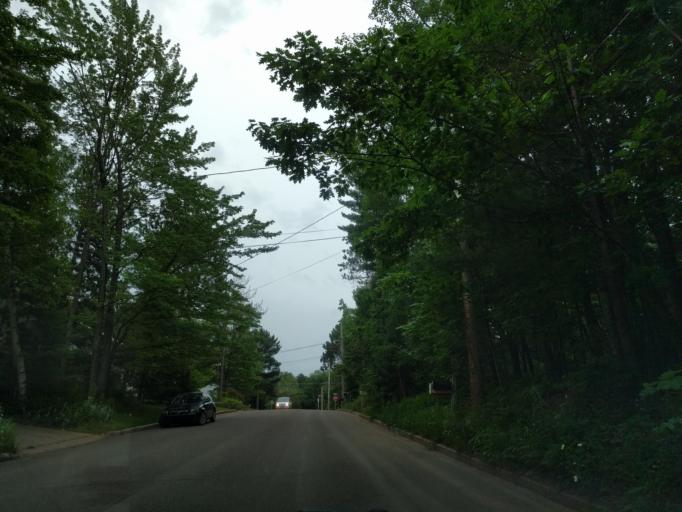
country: US
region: Michigan
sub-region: Marquette County
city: Trowbridge Park
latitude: 46.5613
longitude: -87.4170
